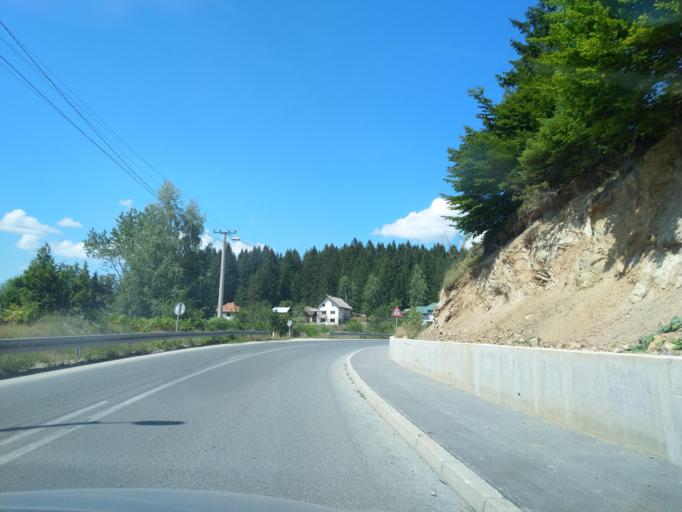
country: RS
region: Central Serbia
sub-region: Zlatiborski Okrug
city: Nova Varos
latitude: 43.4418
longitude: 19.8203
